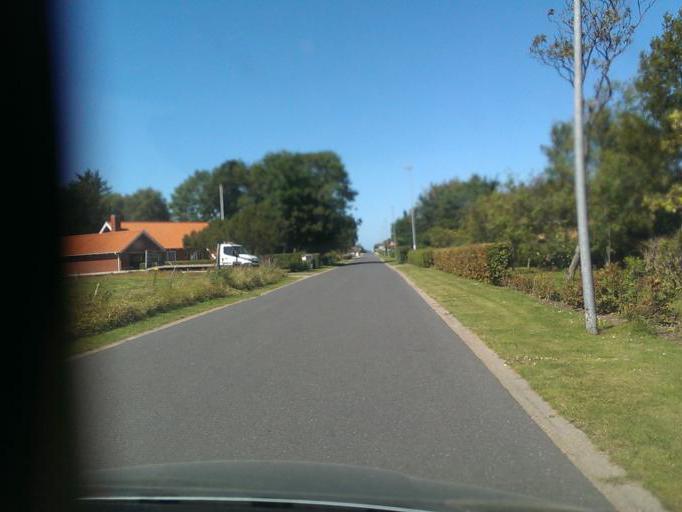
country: DK
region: North Denmark
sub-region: Jammerbugt Kommune
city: Pandrup
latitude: 57.3111
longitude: 9.7175
